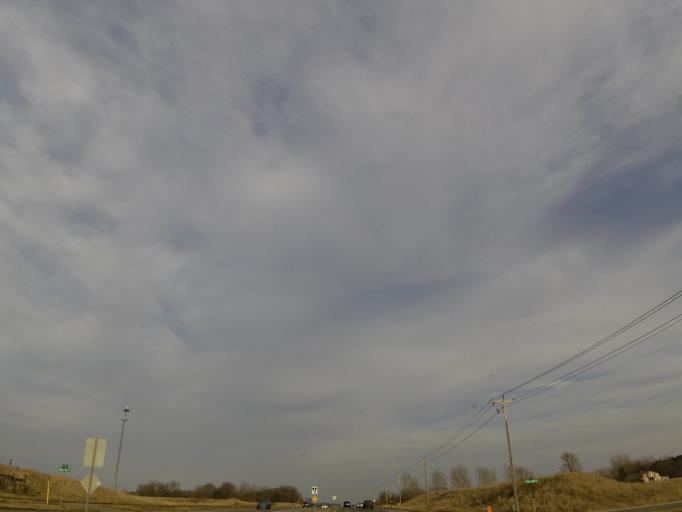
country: US
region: Minnesota
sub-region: Dakota County
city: Lakeville
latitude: 44.6814
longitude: -93.3268
